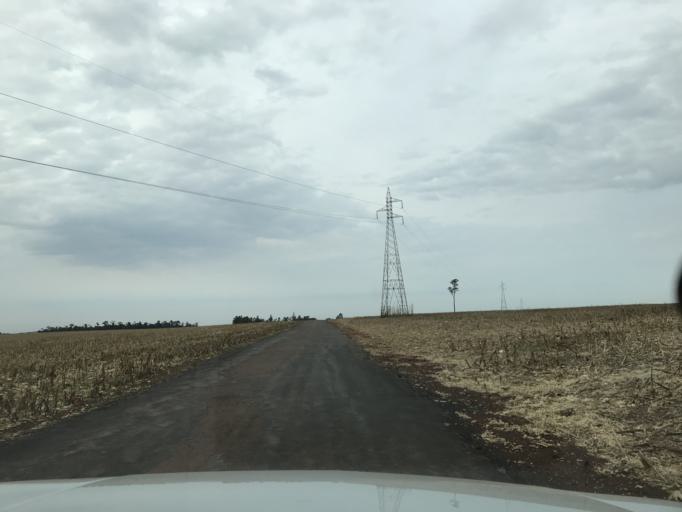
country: BR
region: Parana
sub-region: Palotina
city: Palotina
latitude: -24.2848
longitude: -53.7899
